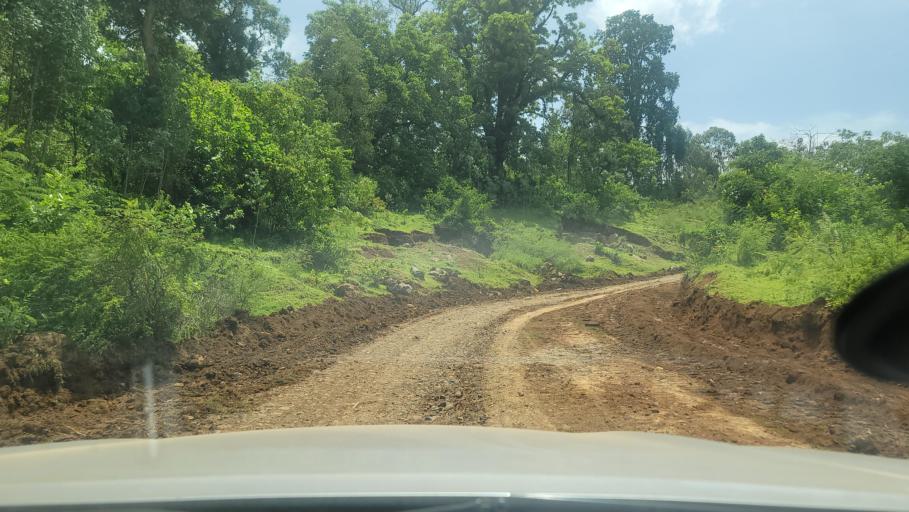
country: ET
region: Southern Nations, Nationalities, and People's Region
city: Bonga
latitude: 7.6878
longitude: 36.2426
